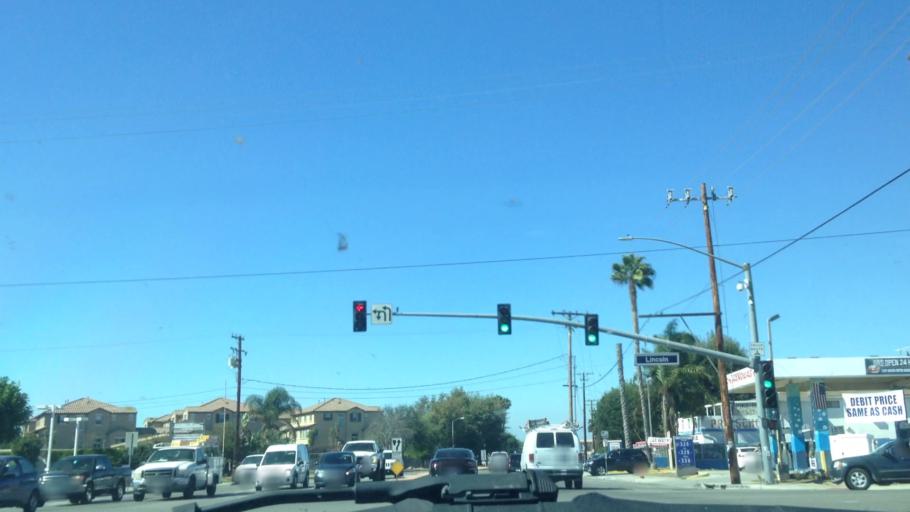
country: US
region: California
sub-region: Orange County
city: Placentia
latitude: 33.8355
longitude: -117.8524
